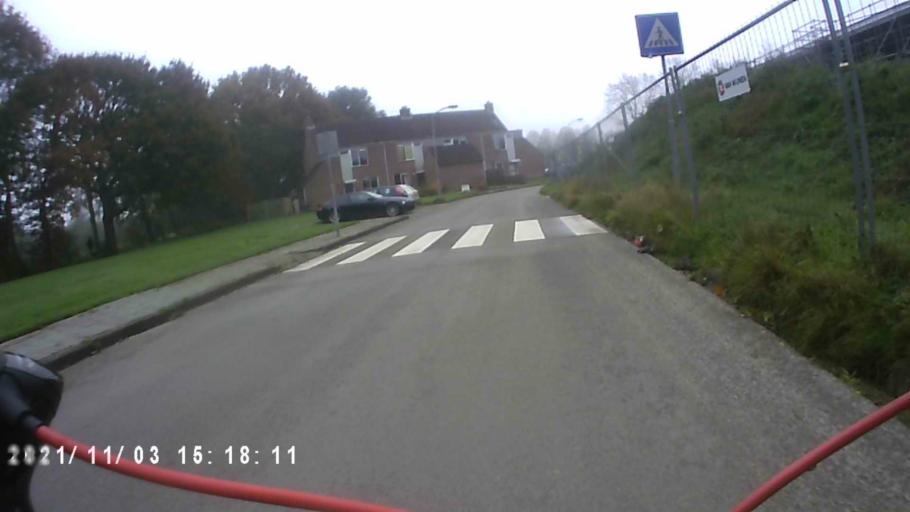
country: NL
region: Groningen
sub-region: Gemeente Leek
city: Leek
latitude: 53.1626
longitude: 6.3621
